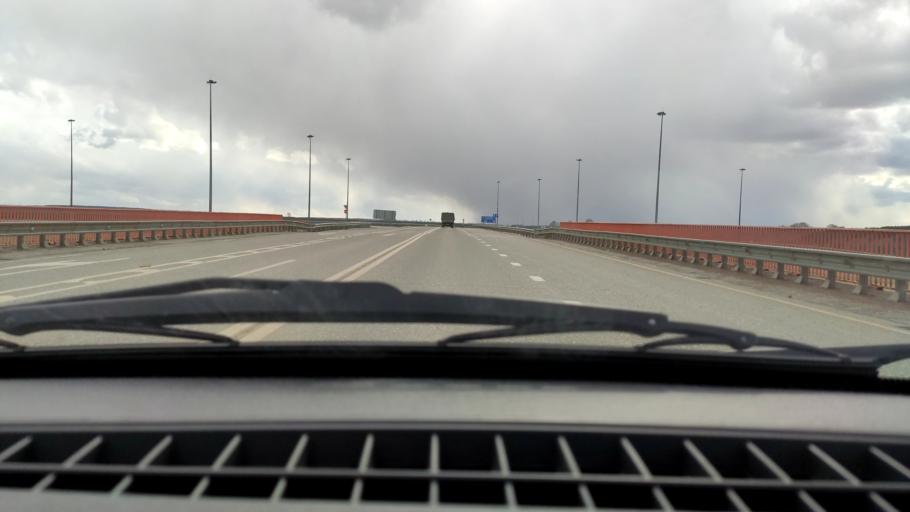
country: RU
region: Bashkortostan
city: Kushnarenkovo
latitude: 55.0780
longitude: 55.2761
